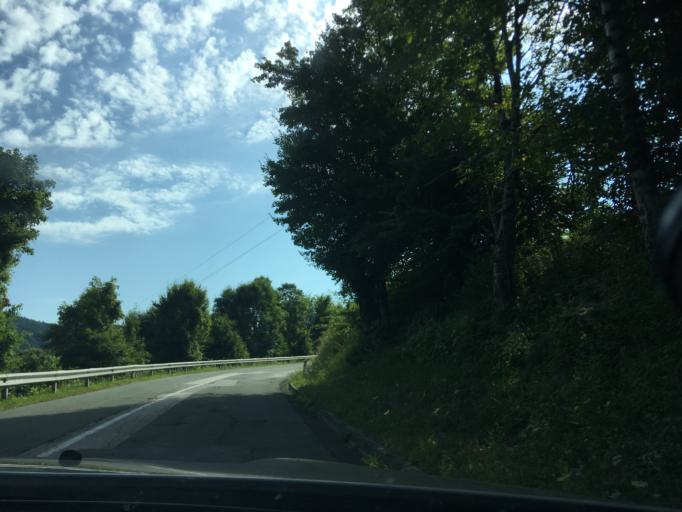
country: HR
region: Primorsko-Goranska
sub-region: Grad Delnice
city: Delnice
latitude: 45.4357
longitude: 14.8489
